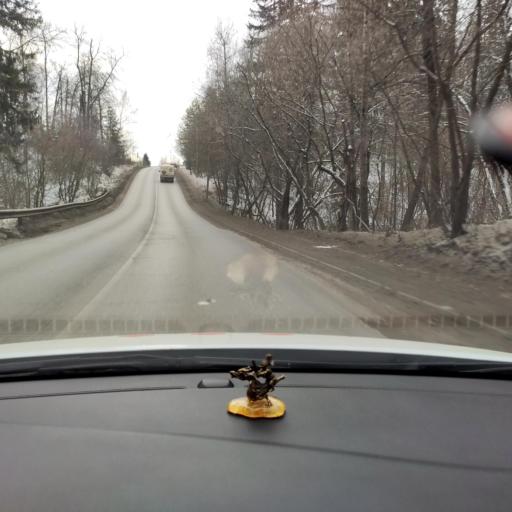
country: RU
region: Tatarstan
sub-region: Zelenodol'skiy Rayon
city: Zelenodolsk
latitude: 55.8613
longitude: 48.5342
